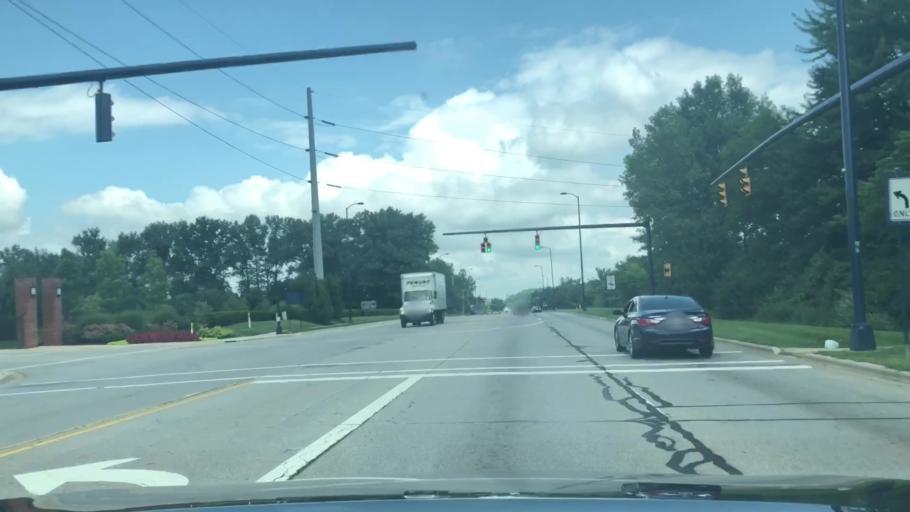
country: US
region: Ohio
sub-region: Franklin County
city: Gahanna
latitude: 40.0366
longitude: -82.9098
